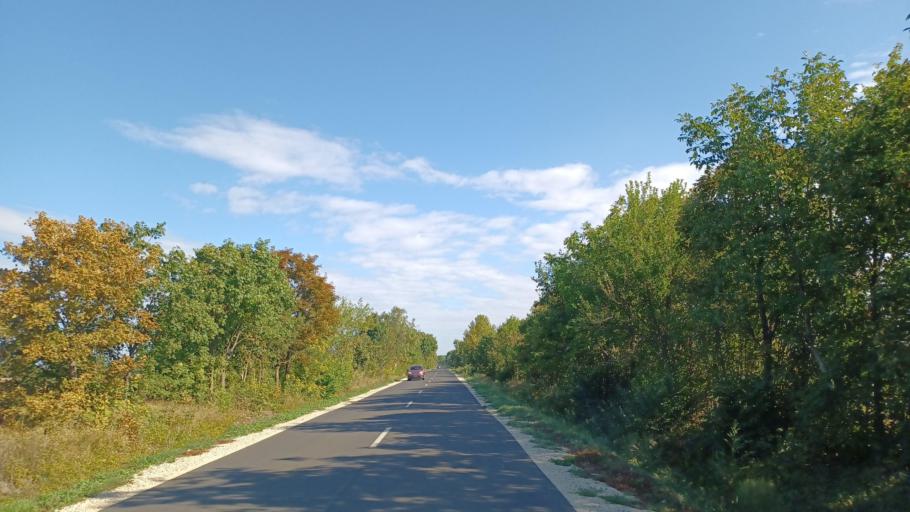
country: HU
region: Tolna
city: Dunaszentgyorgy
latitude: 46.5103
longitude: 18.8244
